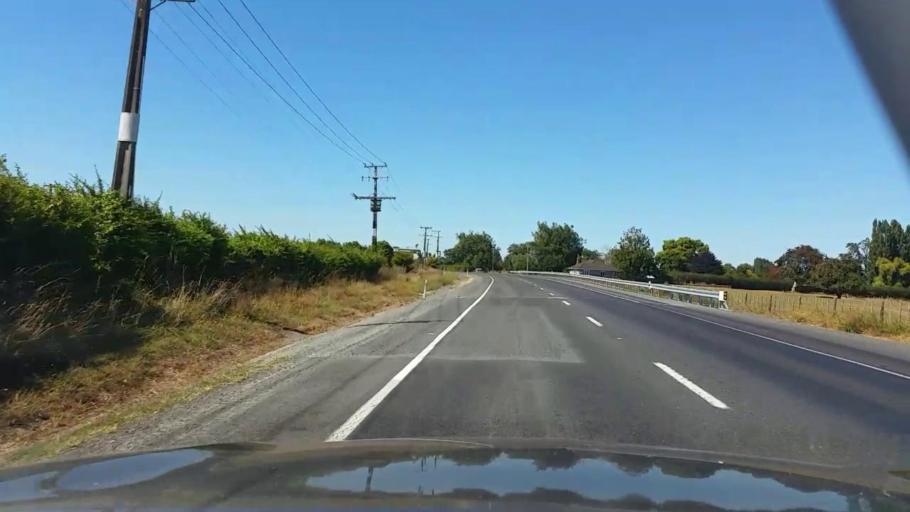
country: NZ
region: Waikato
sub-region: Hamilton City
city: Hamilton
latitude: -37.6639
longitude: 175.2987
